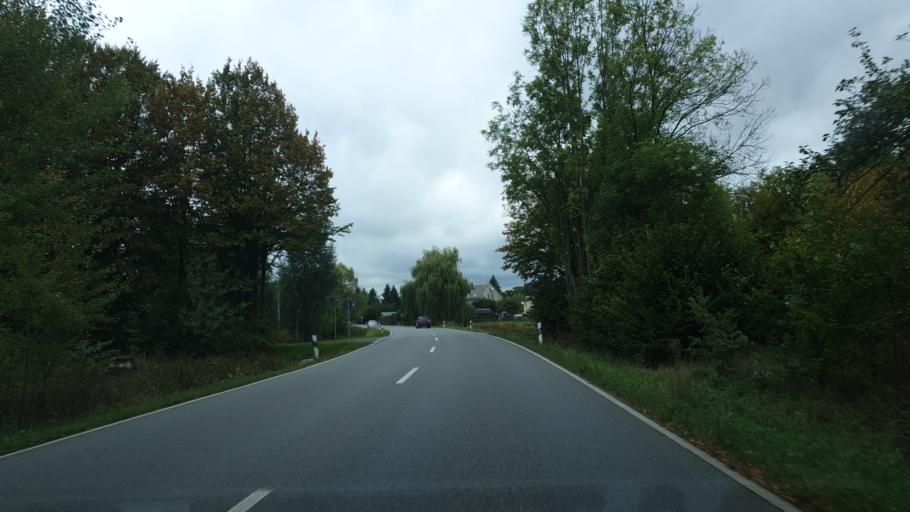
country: DE
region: Saxony
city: Glauchau
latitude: 50.8170
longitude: 12.5695
